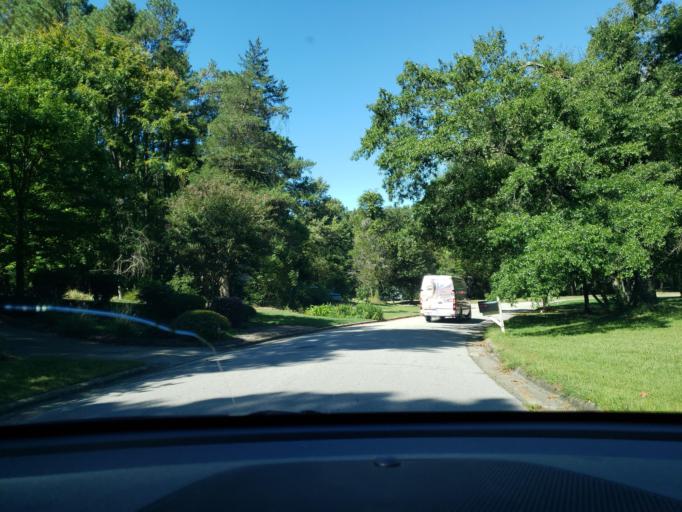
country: US
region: North Carolina
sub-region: Durham County
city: Durham
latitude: 35.9152
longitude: -78.9430
